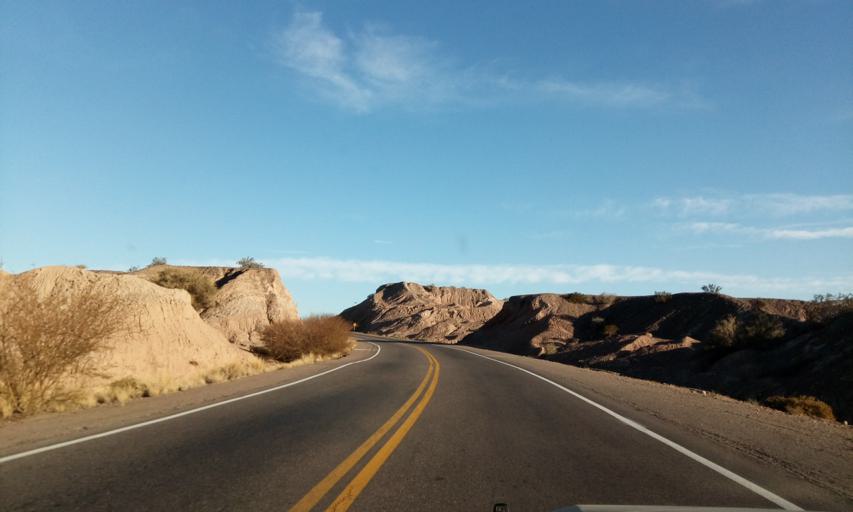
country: AR
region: San Juan
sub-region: Departamento de Rivadavia
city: Rivadavia
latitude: -31.4610
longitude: -68.6402
